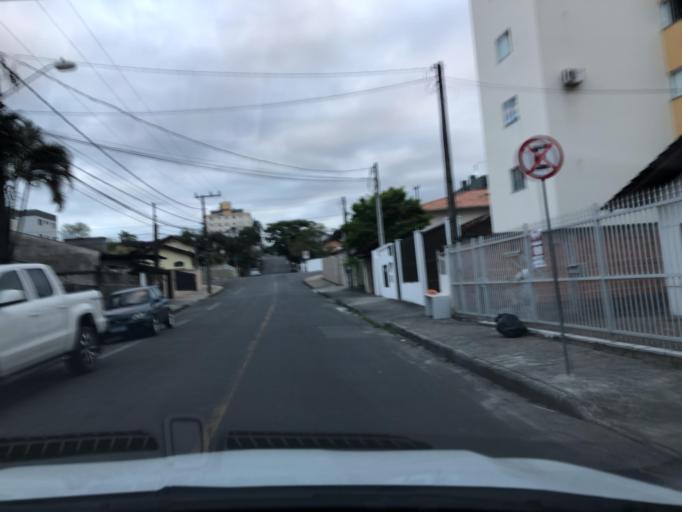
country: BR
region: Santa Catarina
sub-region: Joinville
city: Joinville
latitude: -26.2757
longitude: -48.8714
